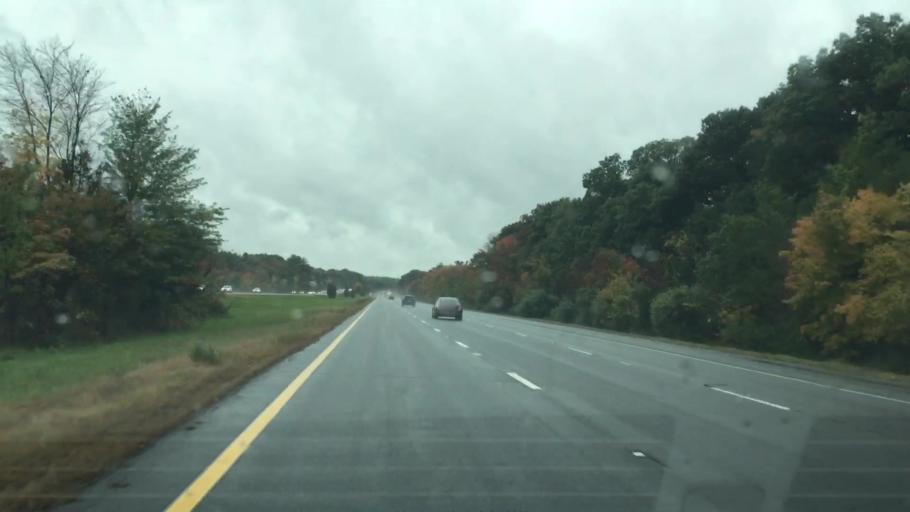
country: US
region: Massachusetts
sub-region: Essex County
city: Amesbury
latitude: 42.8384
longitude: -70.9446
